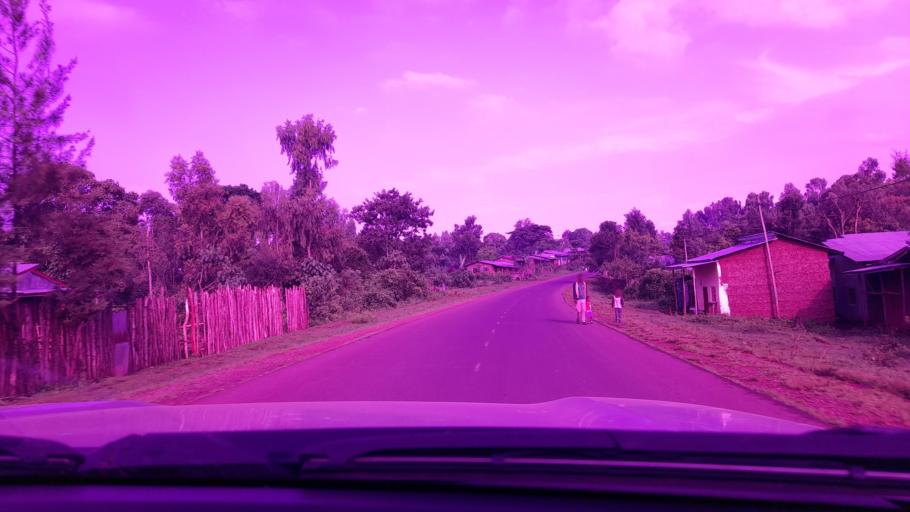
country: ET
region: Oromiya
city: Bedele
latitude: 8.1679
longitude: 36.4685
